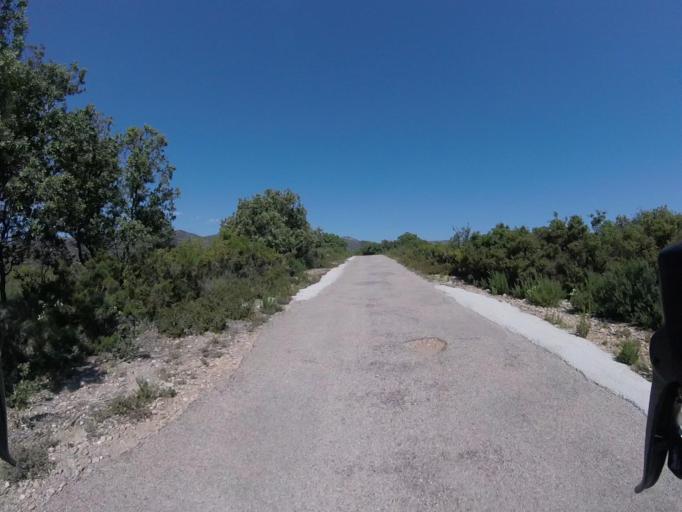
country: ES
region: Valencia
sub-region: Provincia de Castello
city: Sierra-Engarceran
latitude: 40.2329
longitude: -0.0254
